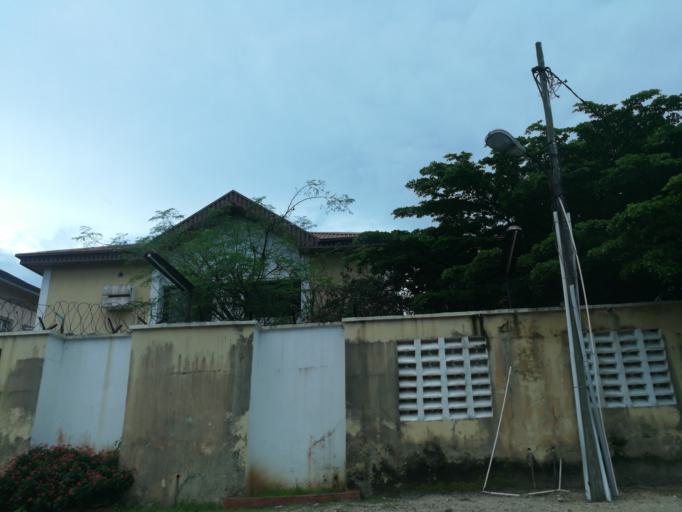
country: NG
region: Lagos
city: Ikoyi
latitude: 6.4459
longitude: 3.4728
